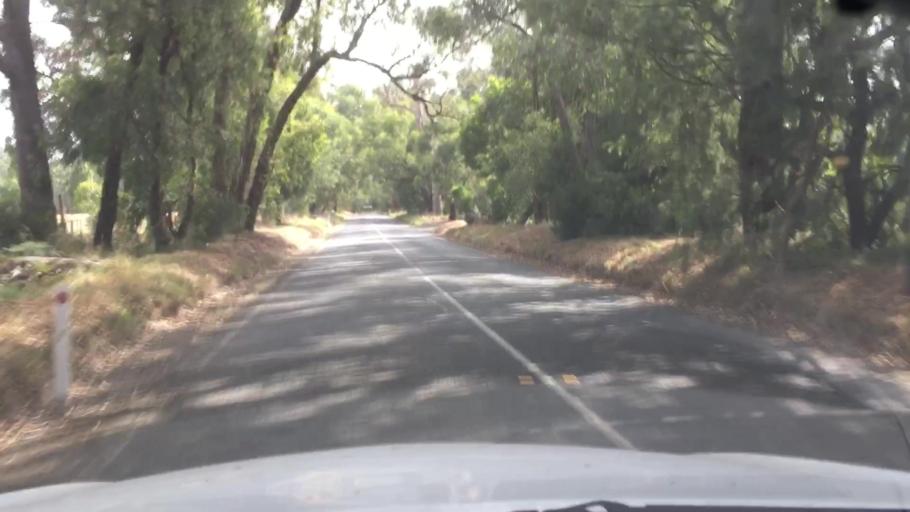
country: AU
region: Victoria
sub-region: Yarra Ranges
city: Woori Yallock
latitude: -37.8172
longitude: 145.4981
